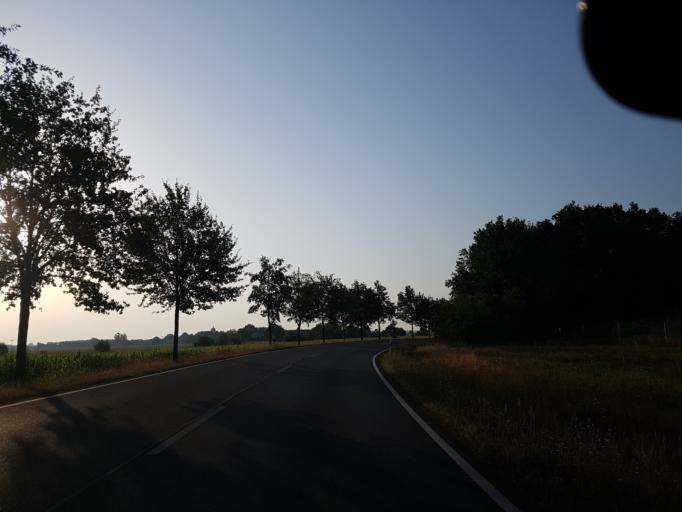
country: DE
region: Saxony
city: Strehla
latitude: 51.3892
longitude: 13.1876
